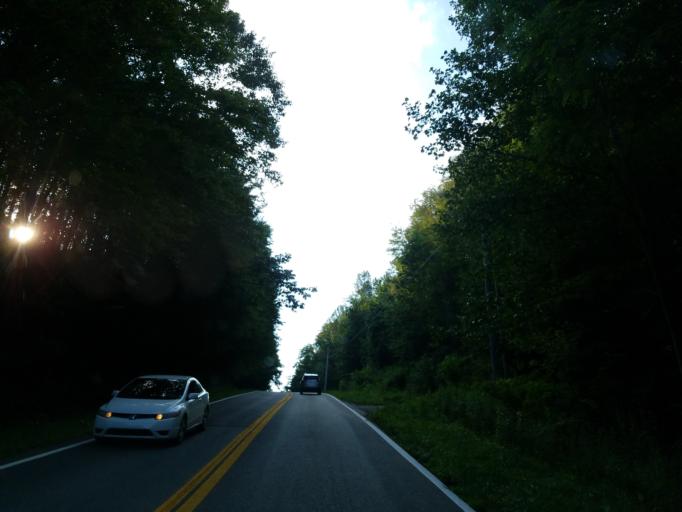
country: US
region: Georgia
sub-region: Fannin County
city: Blue Ridge
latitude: 34.8173
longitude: -84.3002
